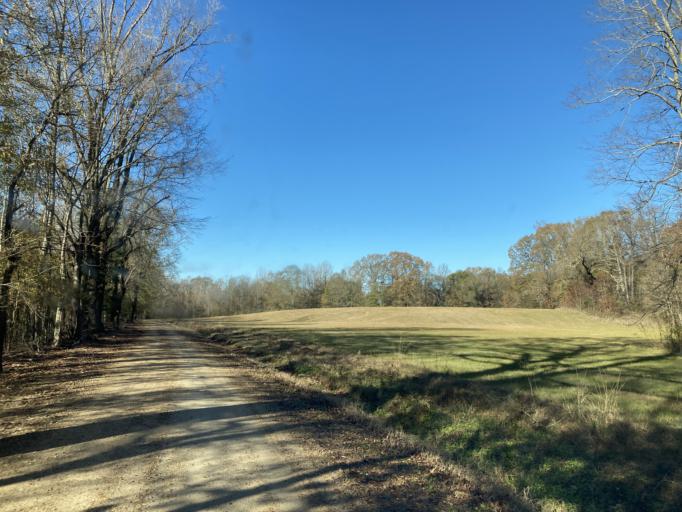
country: US
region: Mississippi
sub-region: Yazoo County
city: Yazoo City
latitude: 32.7133
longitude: -90.4175
